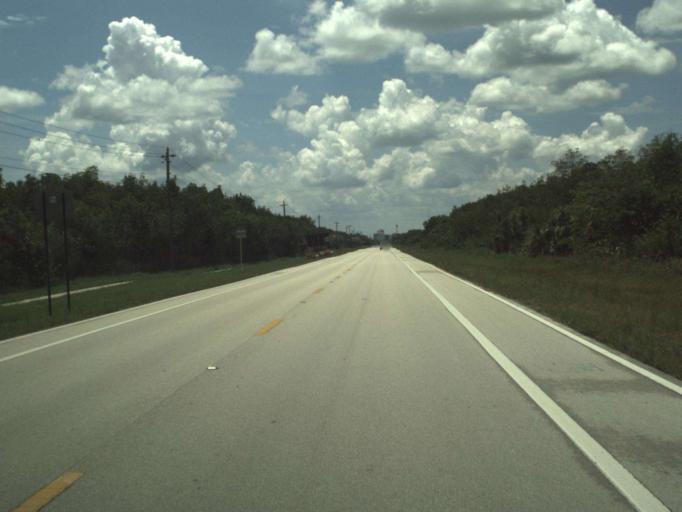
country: US
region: Florida
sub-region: Saint Lucie County
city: Hutchinson Island South
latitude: 27.3370
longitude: -80.2358
